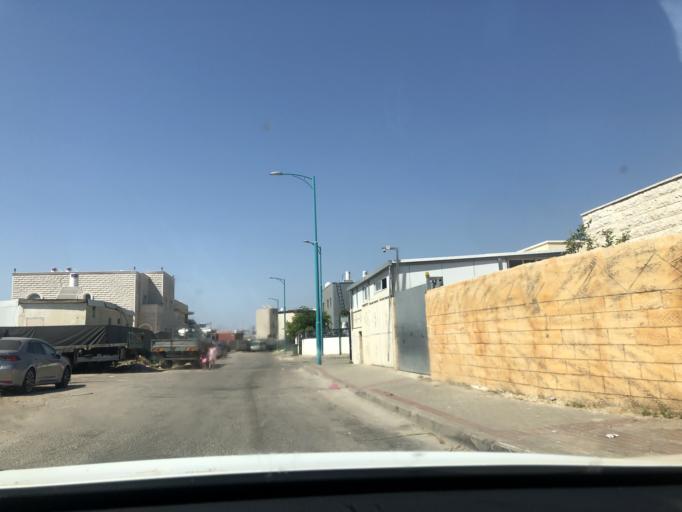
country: IL
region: Central District
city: Lod
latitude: 31.9531
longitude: 34.8744
